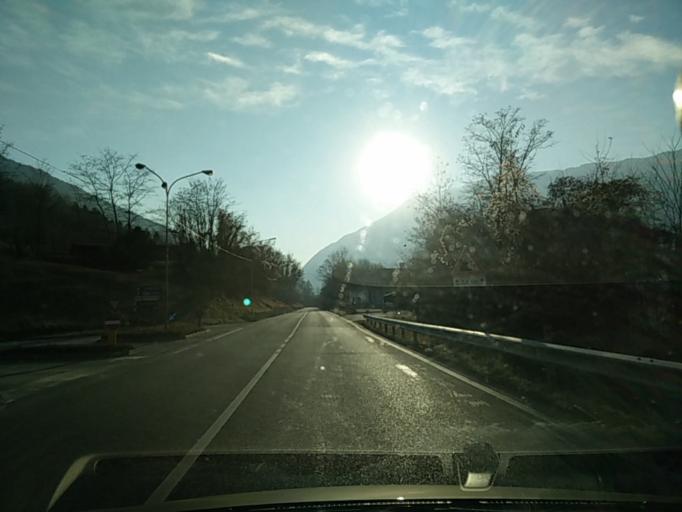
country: IT
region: Veneto
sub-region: Provincia di Belluno
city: Farra d'Alpago
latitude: 46.1157
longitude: 12.3569
